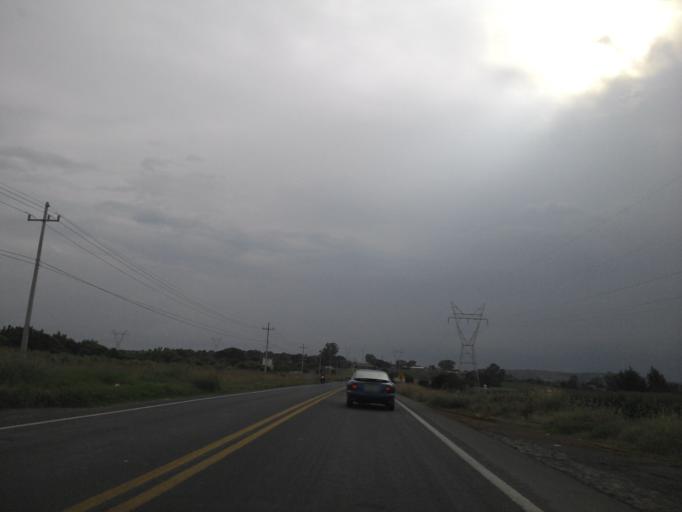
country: MX
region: Jalisco
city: Acatic
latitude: 20.7073
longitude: -102.9575
